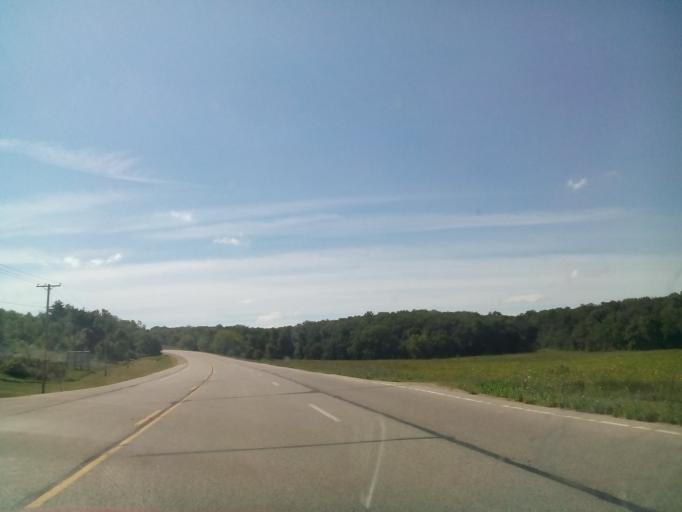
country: US
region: Wisconsin
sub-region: Green County
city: New Glarus
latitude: 42.7972
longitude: -89.6326
